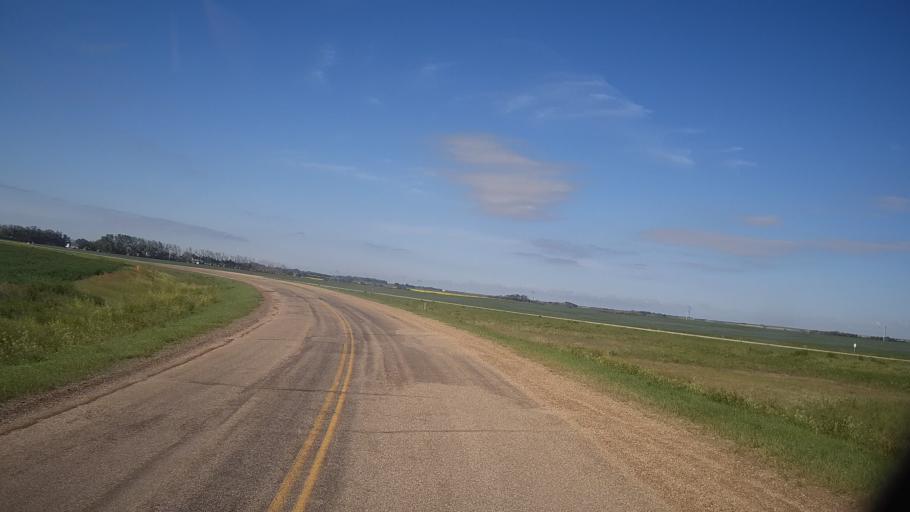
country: CA
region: Saskatchewan
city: Watrous
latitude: 51.8226
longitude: -105.2854
